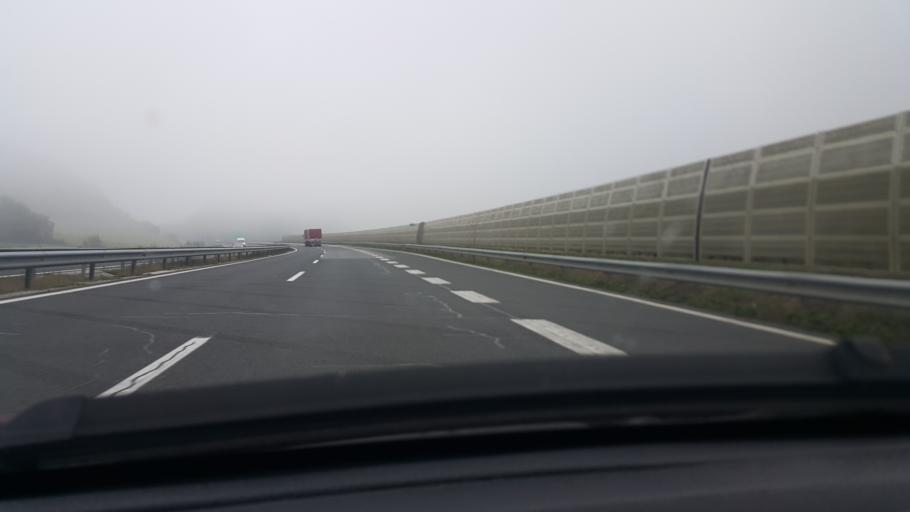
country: SI
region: Ivancna Gorica
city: Sentvid pri Sticni
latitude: 45.9234
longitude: 14.8934
